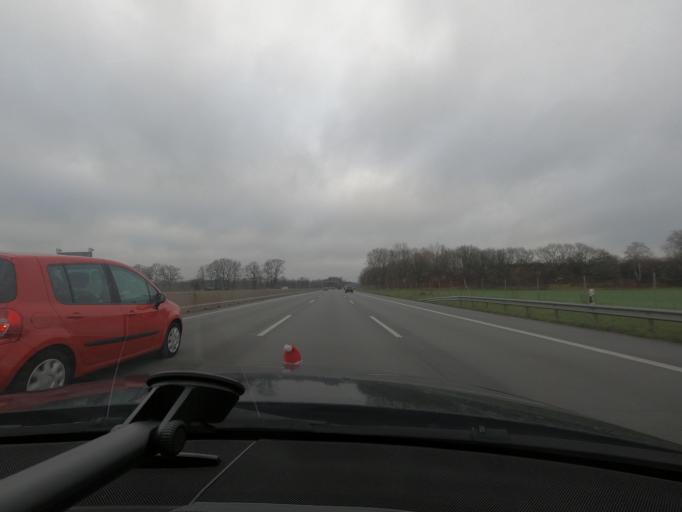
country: DE
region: Schleswig-Holstein
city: Bonningstedt
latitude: 53.6551
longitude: 9.9314
